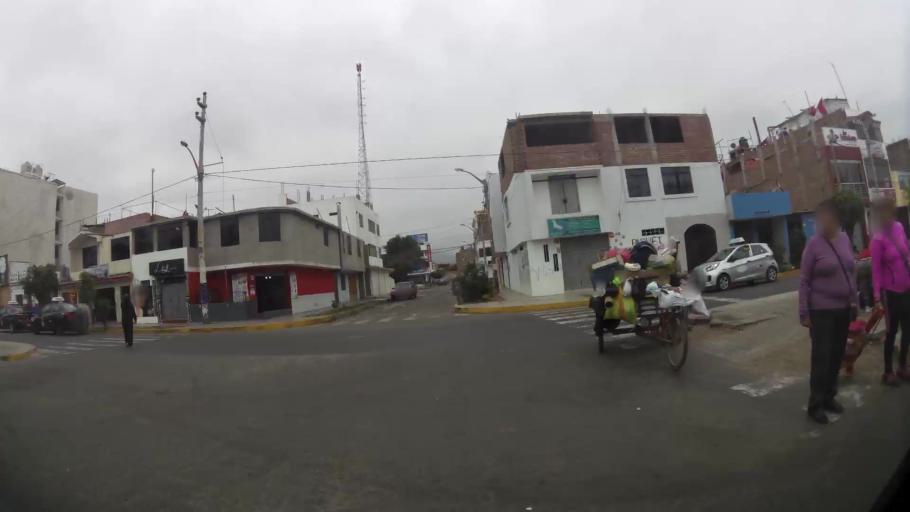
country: PE
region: La Libertad
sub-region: Provincia de Trujillo
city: Trujillo
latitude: -8.1079
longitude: -79.0438
